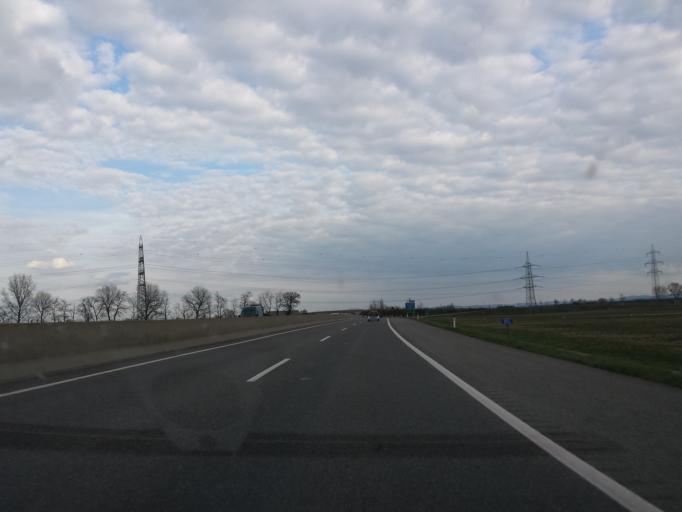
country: AT
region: Lower Austria
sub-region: Politischer Bezirk Tulln
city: Kirchberg am Wagram
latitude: 48.4090
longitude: 15.8734
